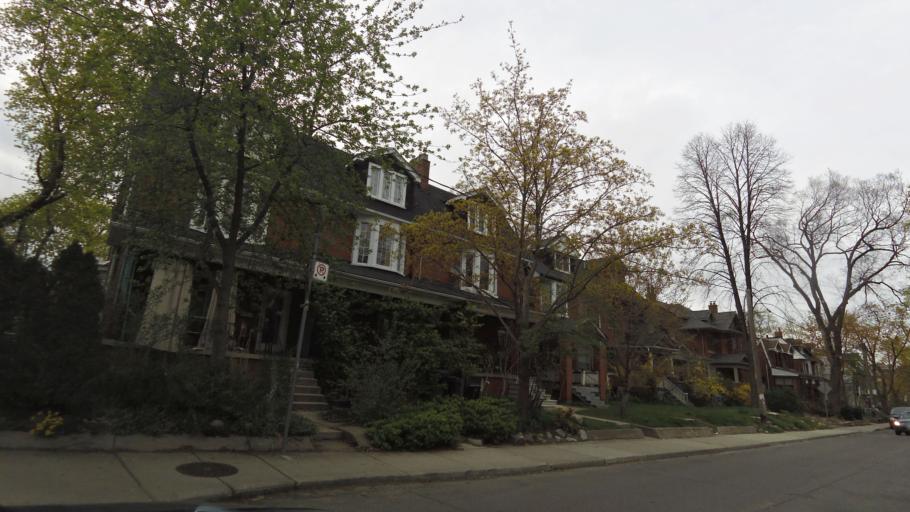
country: CA
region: Ontario
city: Toronto
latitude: 43.6668
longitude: -79.4184
